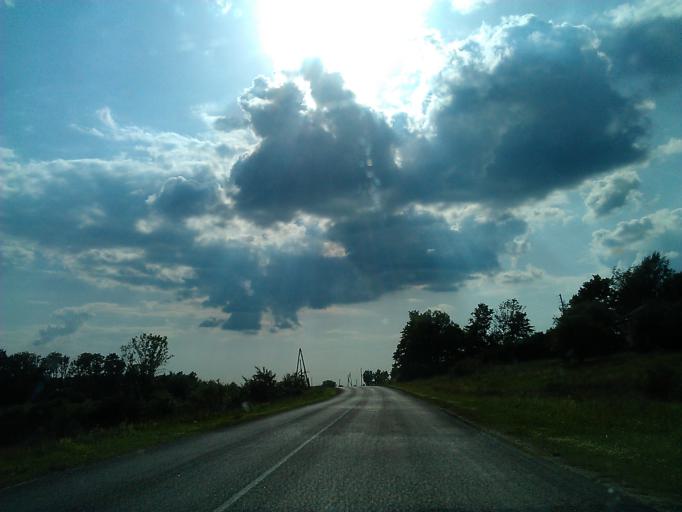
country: LV
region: Aizpute
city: Aizpute
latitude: 56.7190
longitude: 21.6315
